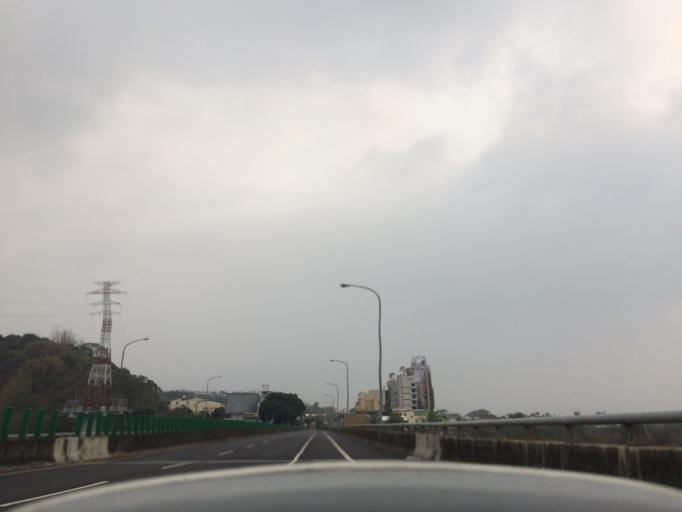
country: TW
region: Taiwan
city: Zhongxing New Village
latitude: 24.0074
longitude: 120.6950
